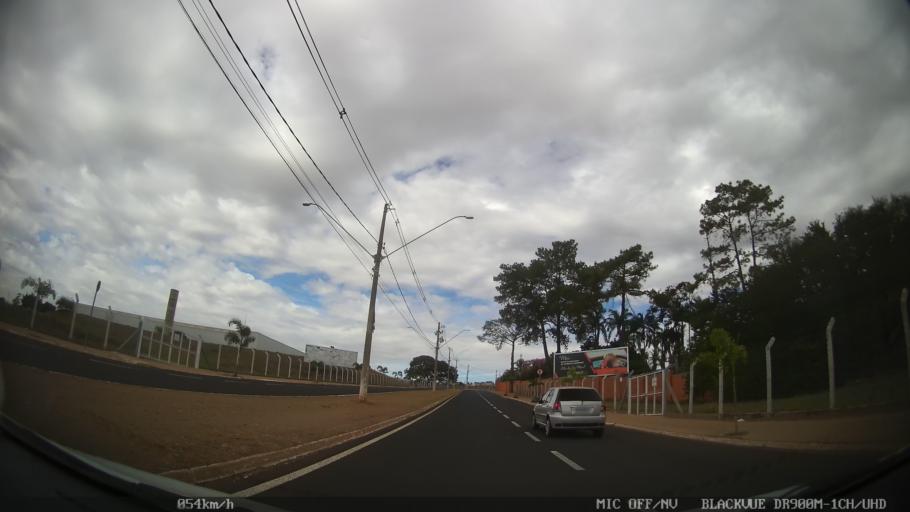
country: BR
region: Sao Paulo
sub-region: Sao Jose Do Rio Preto
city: Sao Jose do Rio Preto
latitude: -20.8159
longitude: -49.4817
